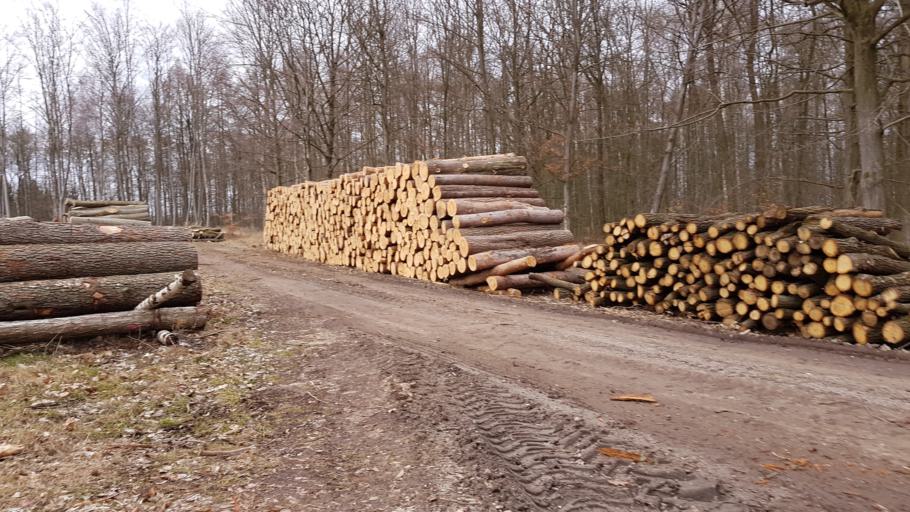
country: PL
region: West Pomeranian Voivodeship
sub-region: Powiat pyrzycki
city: Kozielice
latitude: 53.0835
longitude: 14.7488
